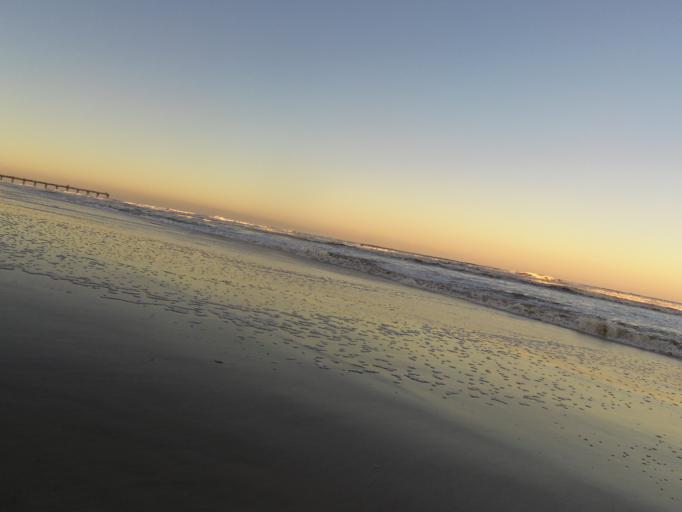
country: US
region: Florida
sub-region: Duval County
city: Jacksonville Beach
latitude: 30.2879
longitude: -81.3879
